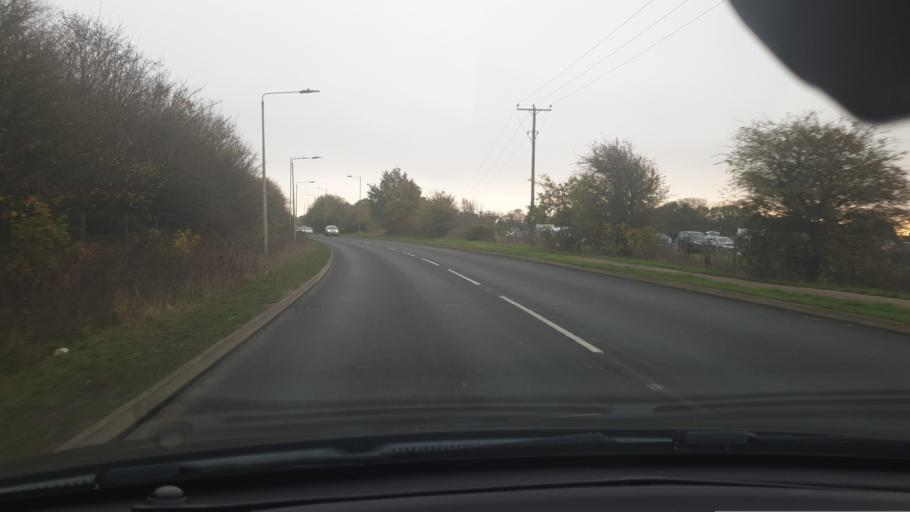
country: GB
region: England
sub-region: Essex
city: Little Clacton
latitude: 51.8203
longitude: 1.1433
